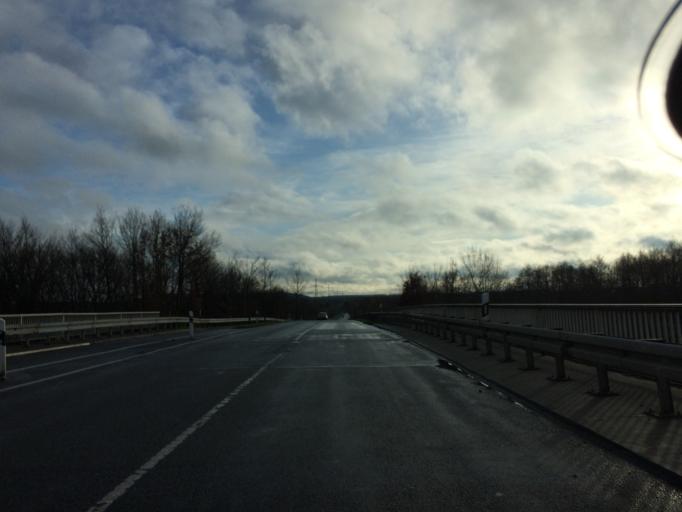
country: DE
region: North Rhine-Westphalia
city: Marl
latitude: 51.7078
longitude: 7.1276
